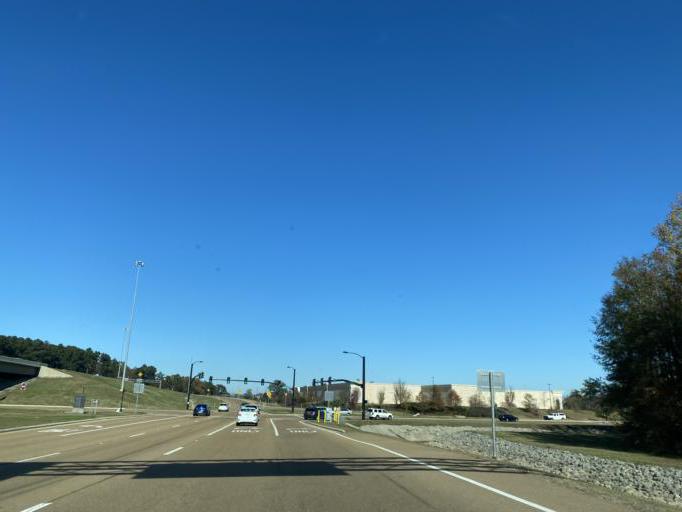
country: US
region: Mississippi
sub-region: Madison County
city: Madison
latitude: 32.4569
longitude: -90.1420
